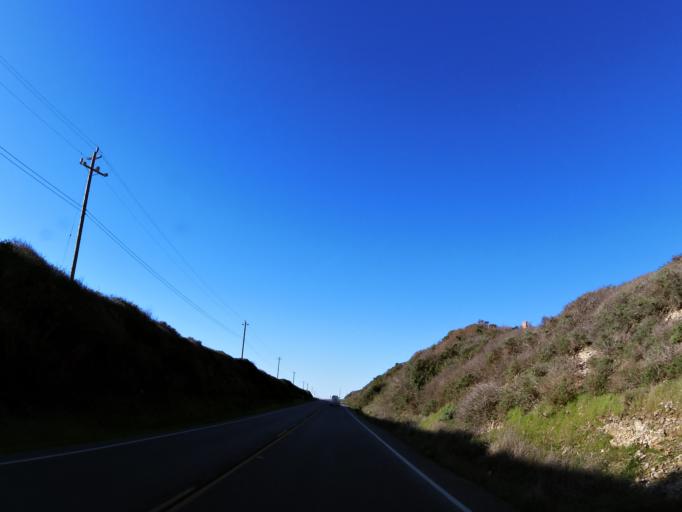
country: US
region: California
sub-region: Santa Cruz County
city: Bonny Doon
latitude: 36.9940
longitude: -122.1697
